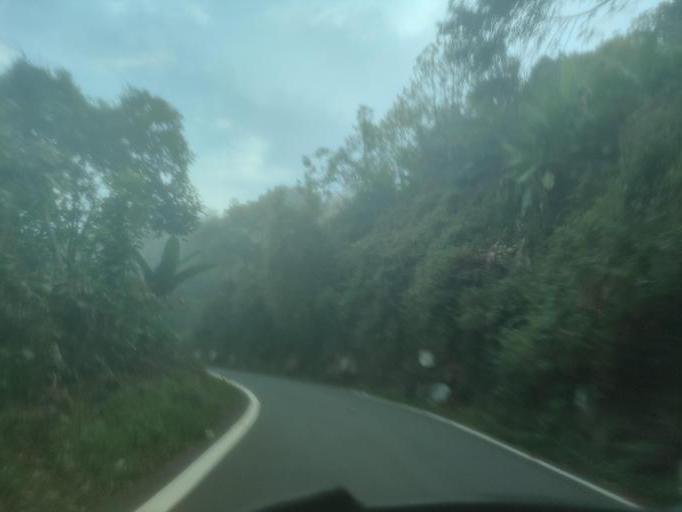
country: IN
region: Tamil Nadu
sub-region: Dindigul
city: Kodaikanal
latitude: 10.3194
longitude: 77.5644
